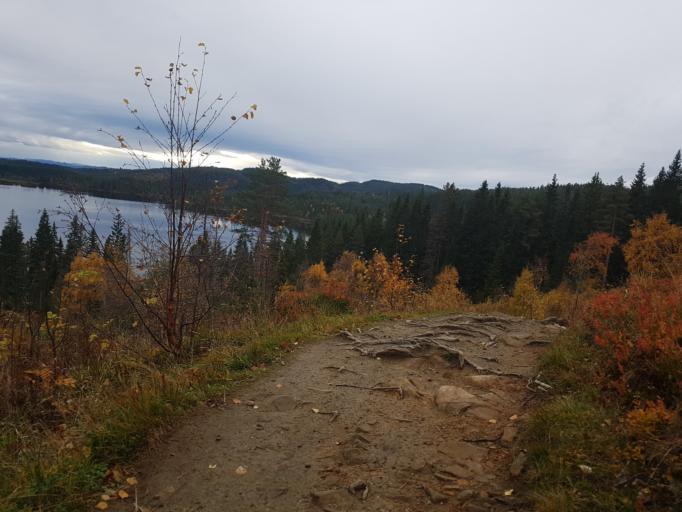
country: NO
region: Sor-Trondelag
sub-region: Melhus
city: Melhus
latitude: 63.4025
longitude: 10.2440
